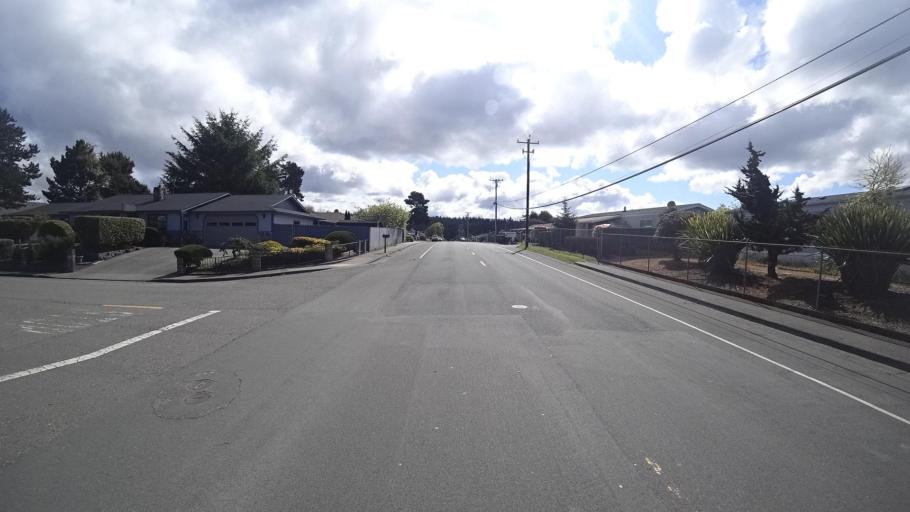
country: US
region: California
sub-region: Humboldt County
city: McKinleyville
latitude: 40.9444
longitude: -124.0972
